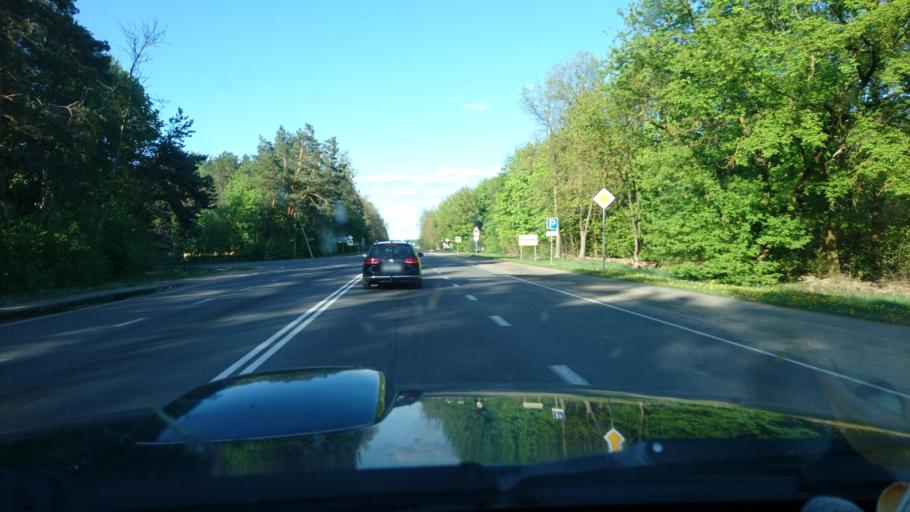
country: BY
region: Brest
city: Byaroza
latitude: 52.5469
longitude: 25.0098
